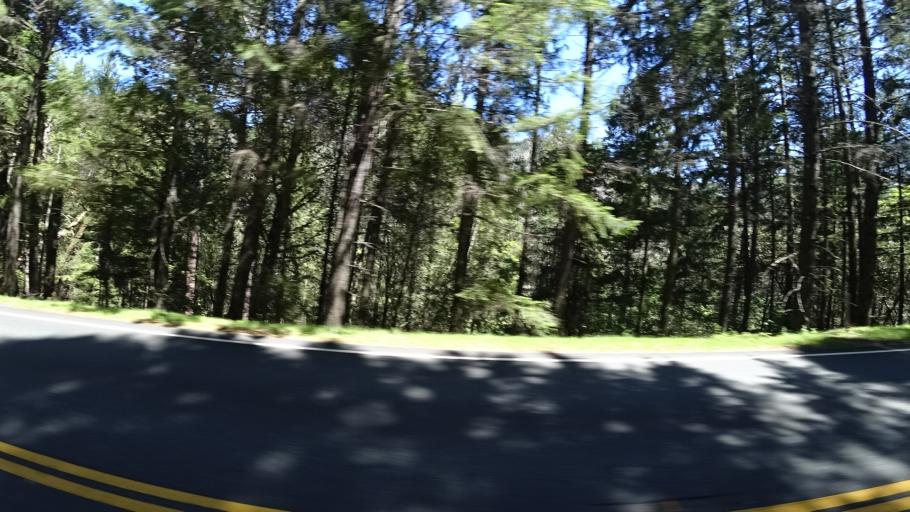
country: US
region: California
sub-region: Humboldt County
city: Willow Creek
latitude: 40.8529
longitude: -123.4889
